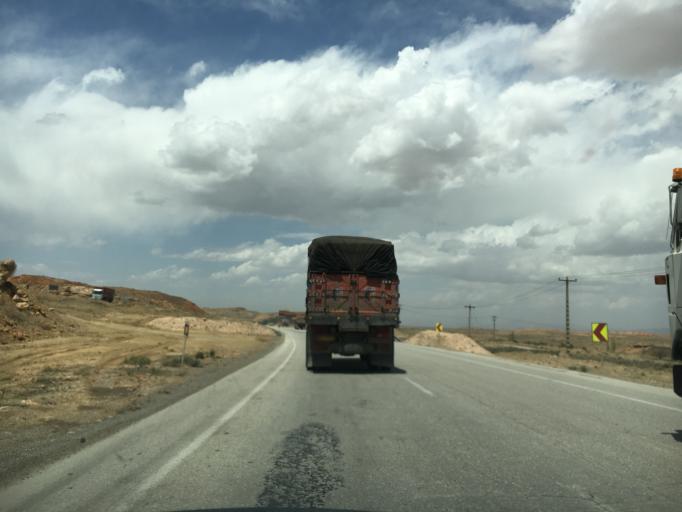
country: IR
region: Markazi
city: Delijan
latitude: 33.6264
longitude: 50.9954
